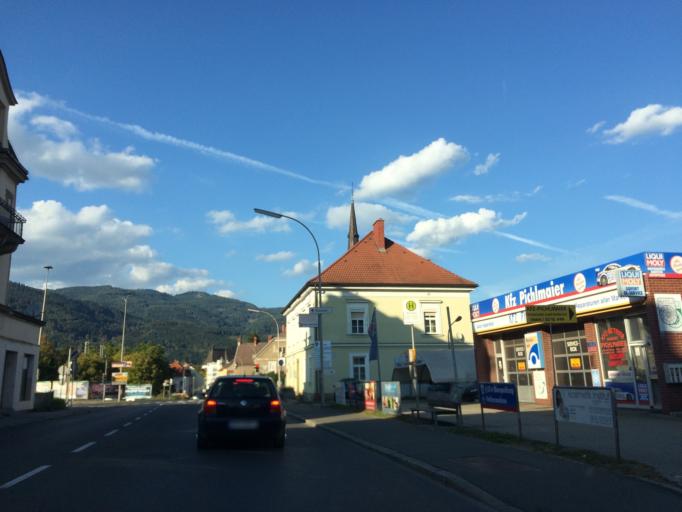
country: AT
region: Styria
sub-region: Politischer Bezirk Leoben
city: Leoben
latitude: 47.3756
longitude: 15.0910
